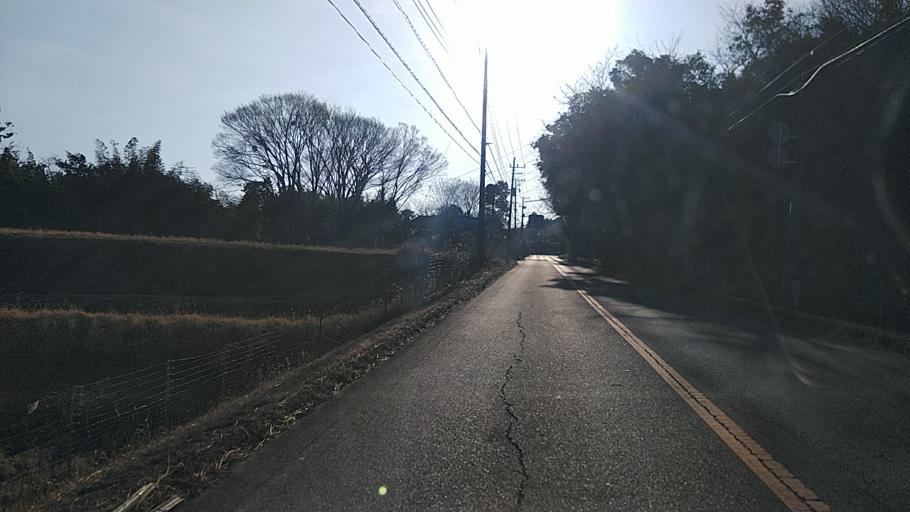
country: JP
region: Chiba
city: Kimitsu
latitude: 35.2891
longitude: 139.9786
